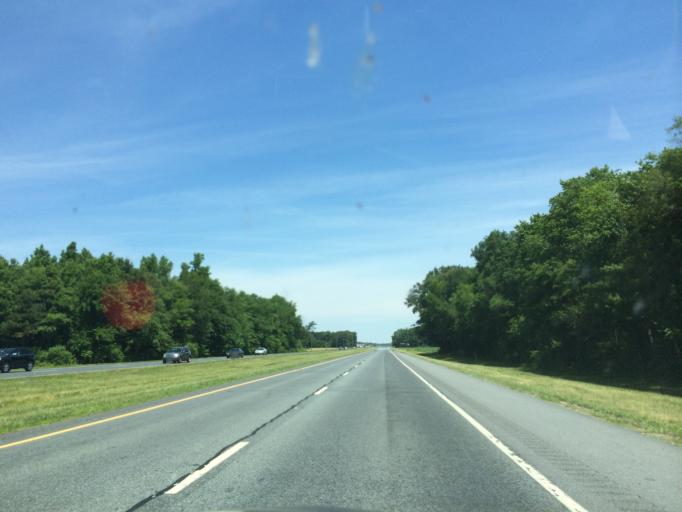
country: US
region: Delaware
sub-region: Sussex County
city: Laurel
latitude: 38.5154
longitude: -75.5569
